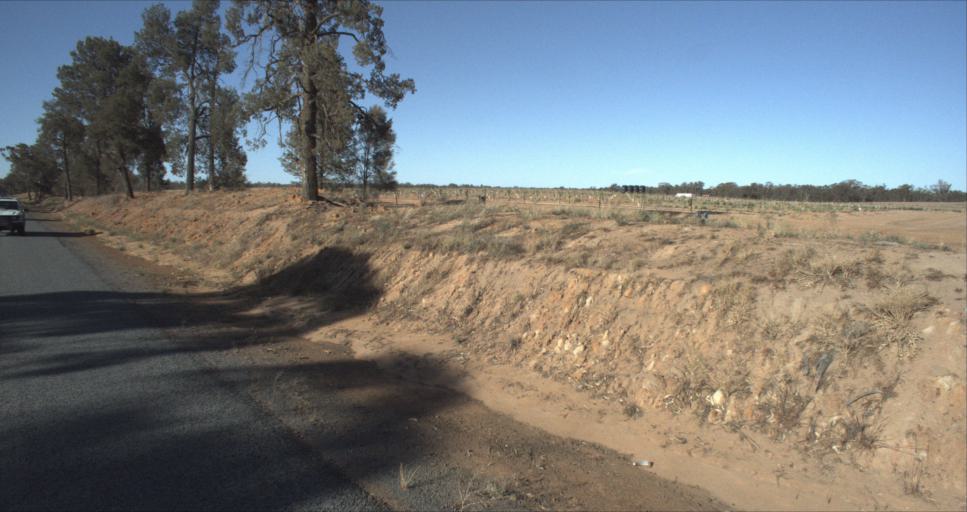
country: AU
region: New South Wales
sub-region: Leeton
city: Leeton
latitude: -34.6524
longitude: 146.3510
